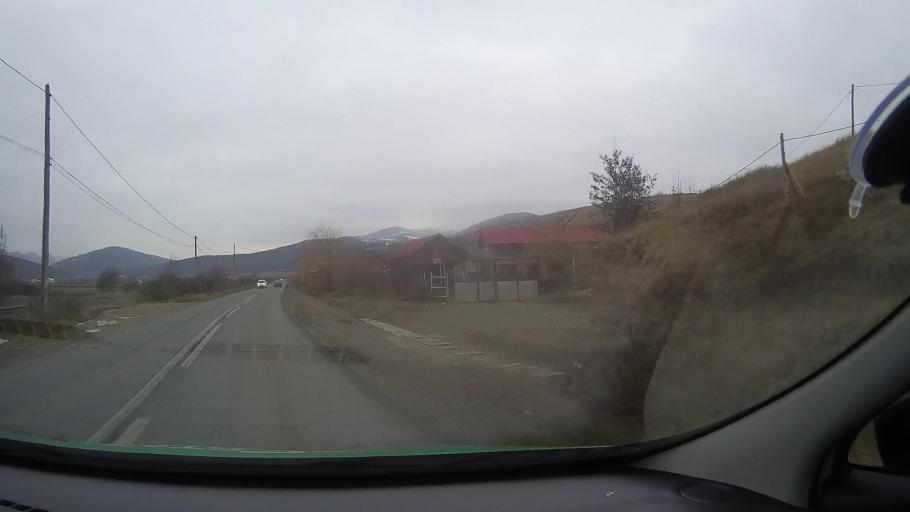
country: RO
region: Alba
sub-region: Comuna Ighiu
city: Sard
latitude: 46.1213
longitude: 23.5099
